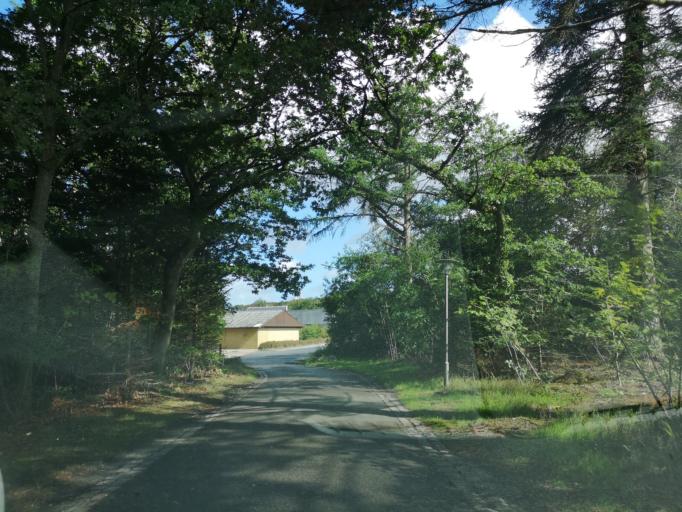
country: DK
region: Central Jutland
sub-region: Holstebro Kommune
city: Holstebro
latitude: 56.3391
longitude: 8.6334
